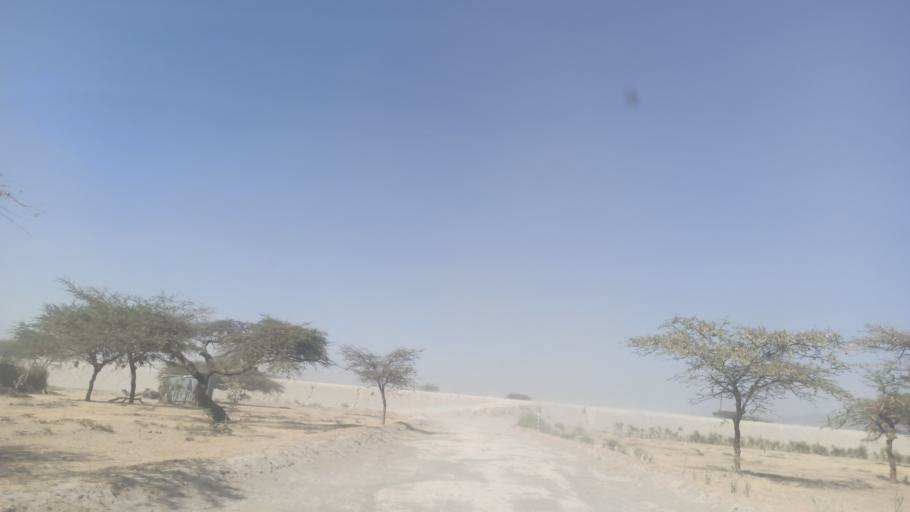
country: ET
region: Oromiya
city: Ziway
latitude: 7.6906
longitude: 38.6563
